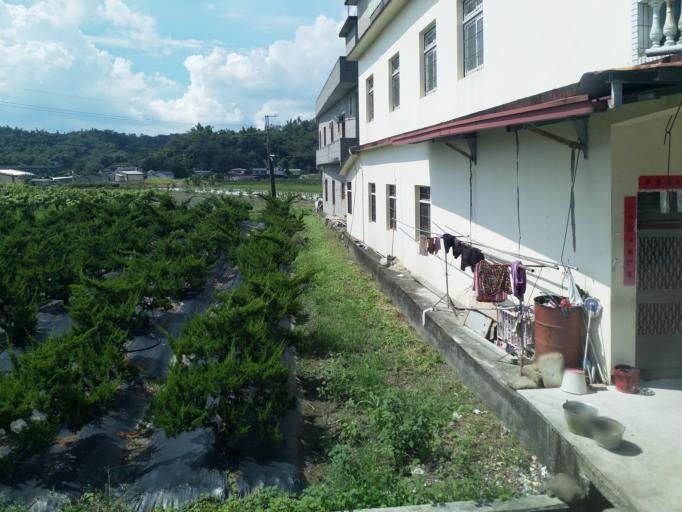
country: TW
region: Taiwan
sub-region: Pingtung
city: Pingtung
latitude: 22.8951
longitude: 120.5797
